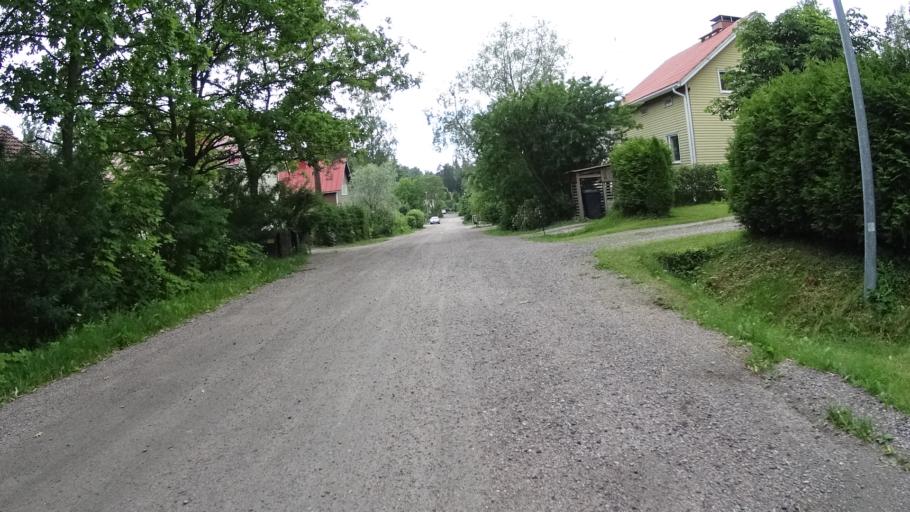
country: FI
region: Uusimaa
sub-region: Helsinki
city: Teekkarikylae
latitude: 60.2503
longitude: 24.8941
